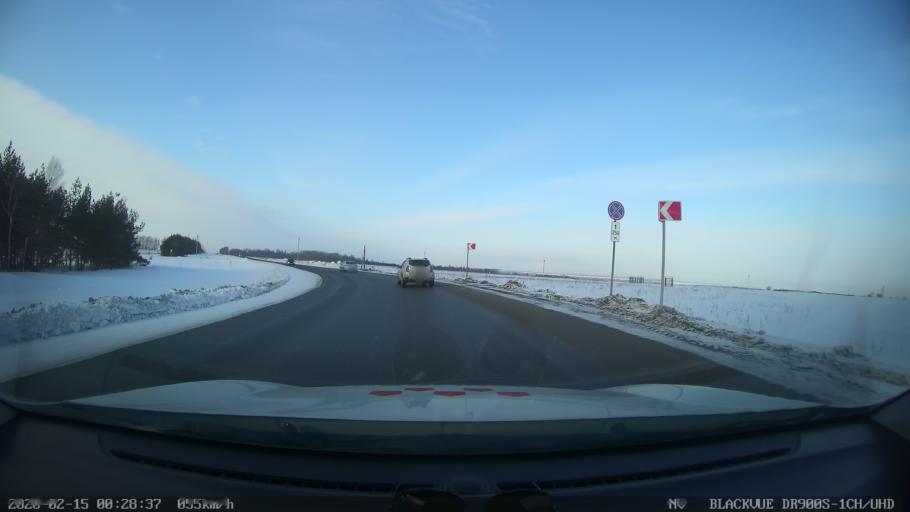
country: RU
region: Tatarstan
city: Verkhniy Uslon
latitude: 55.6441
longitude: 48.8756
